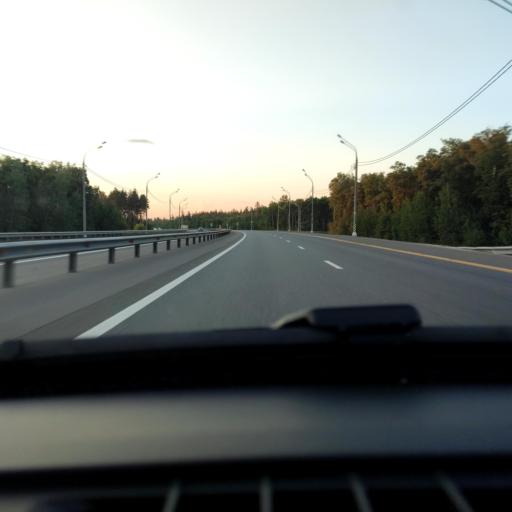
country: RU
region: Lipetsk
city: Khlevnoye
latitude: 52.2514
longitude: 39.0671
